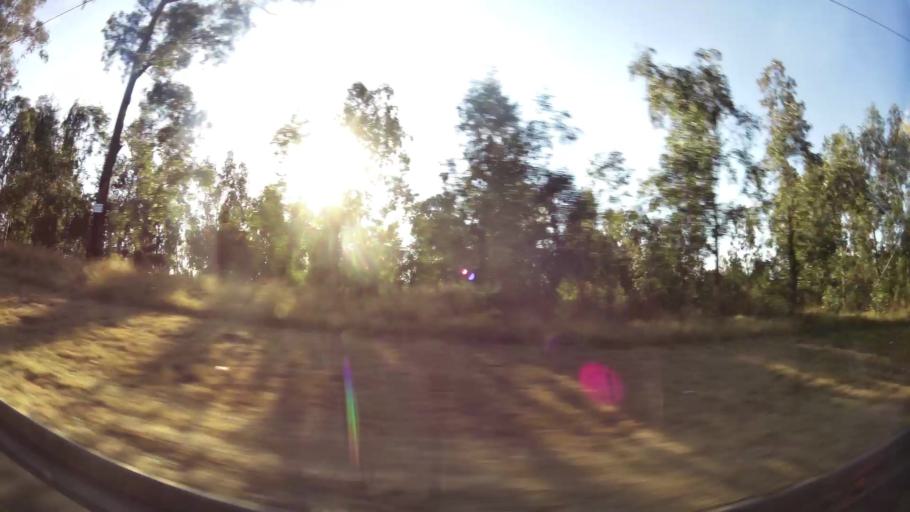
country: ZA
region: Gauteng
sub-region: City of Johannesburg Metropolitan Municipality
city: Johannesburg
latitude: -26.2144
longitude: 27.9867
